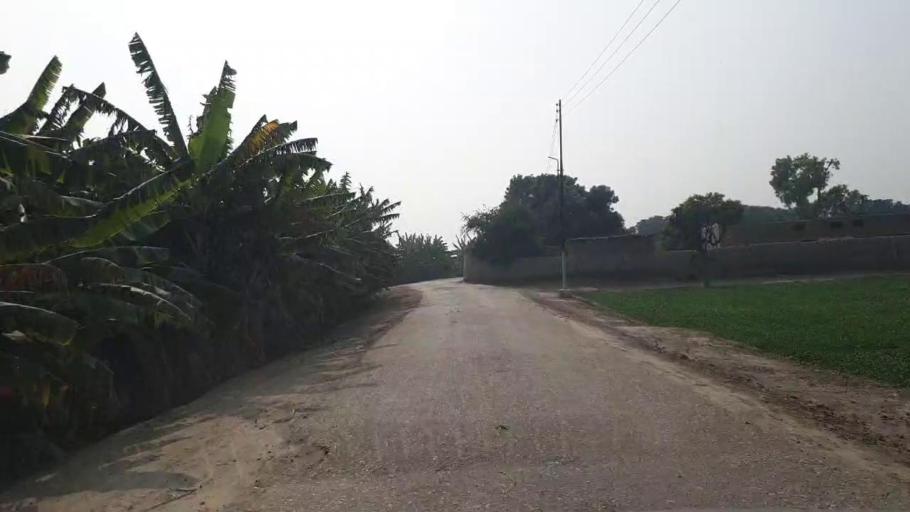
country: PK
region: Sindh
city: Hala
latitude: 25.8201
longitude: 68.4377
